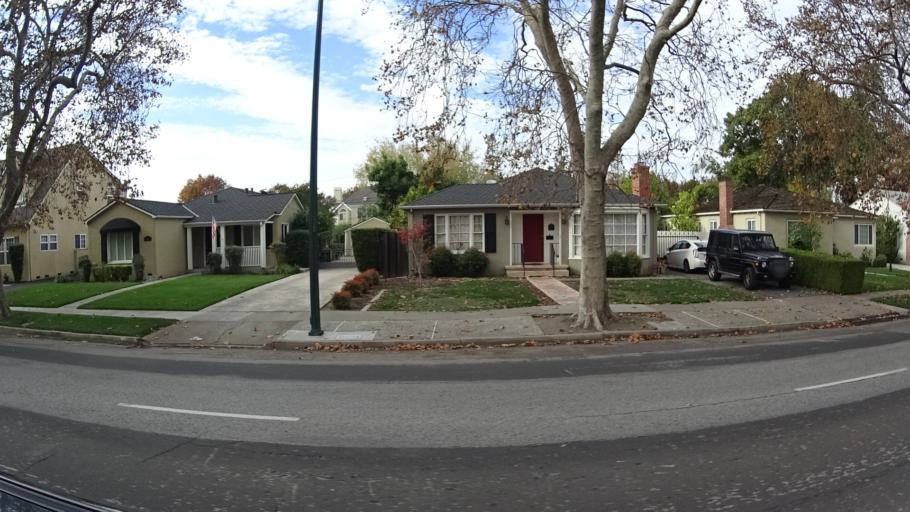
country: US
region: California
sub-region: Santa Clara County
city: Burbank
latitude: 37.3294
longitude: -121.9300
